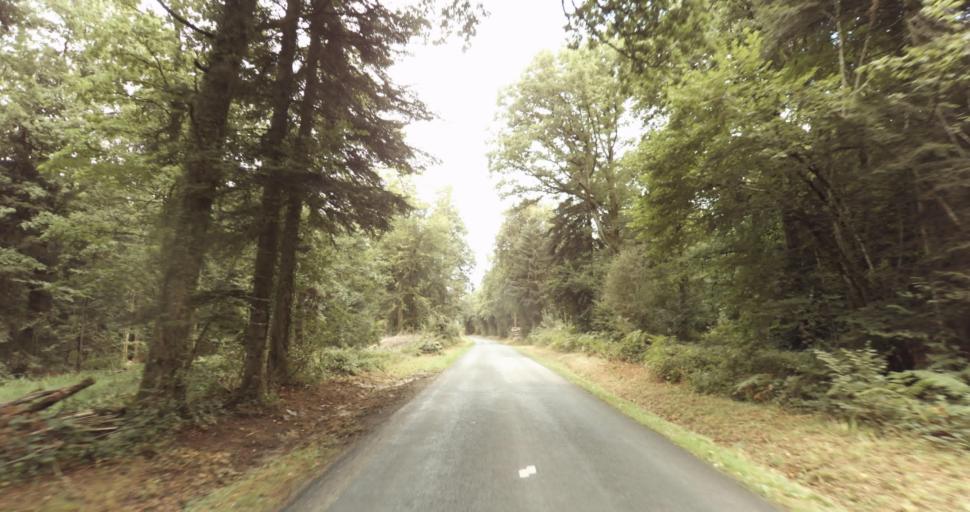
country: FR
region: Lower Normandy
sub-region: Departement de l'Orne
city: Gace
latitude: 48.7994
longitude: 0.2586
